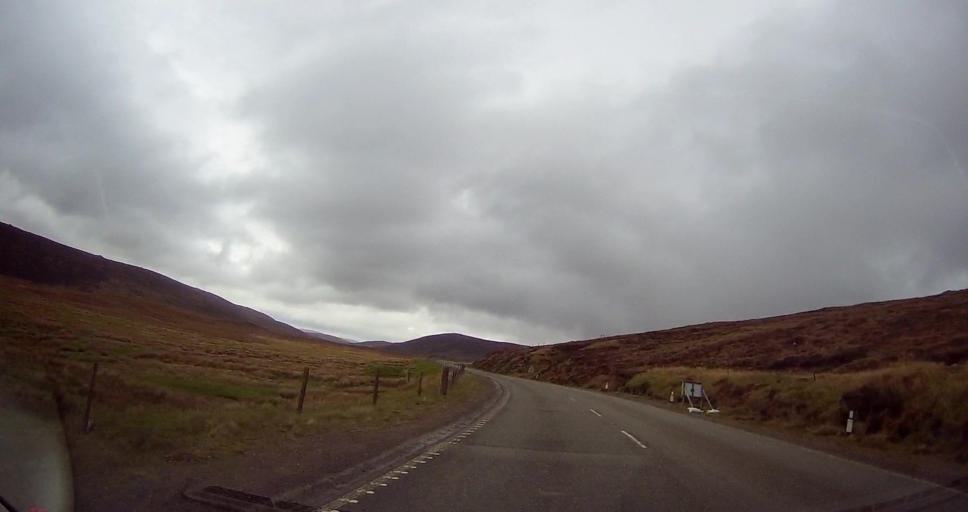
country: GB
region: Scotland
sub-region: Shetland Islands
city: Lerwick
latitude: 60.2862
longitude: -1.2414
